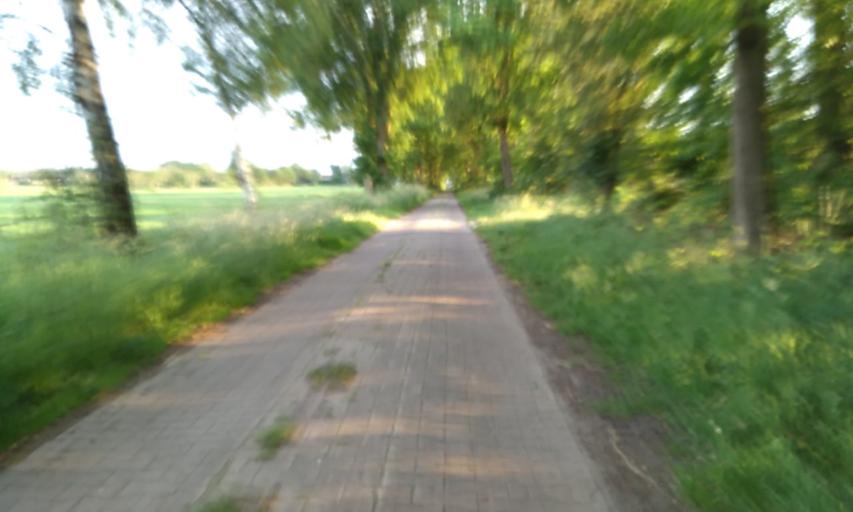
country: DE
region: Lower Saxony
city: Agathenburg
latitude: 53.5285
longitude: 9.4916
